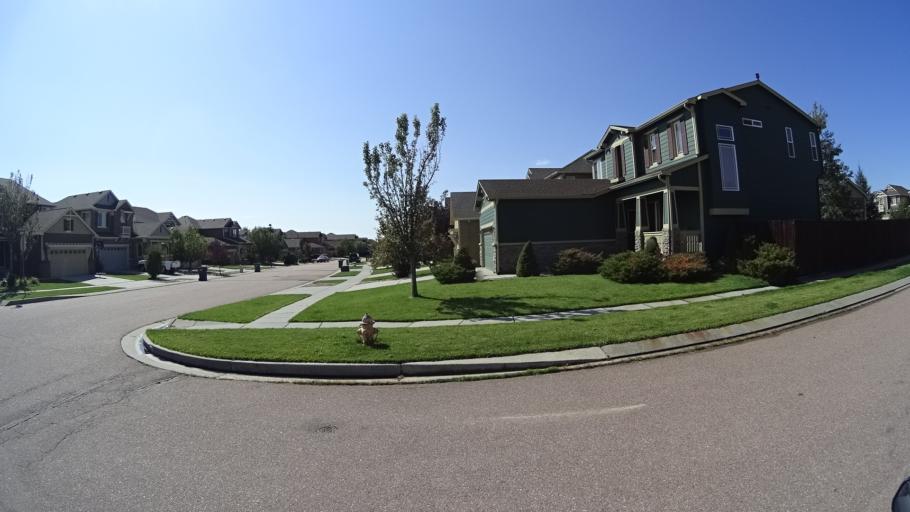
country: US
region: Colorado
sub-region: El Paso County
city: Cimarron Hills
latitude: 38.9296
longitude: -104.7044
